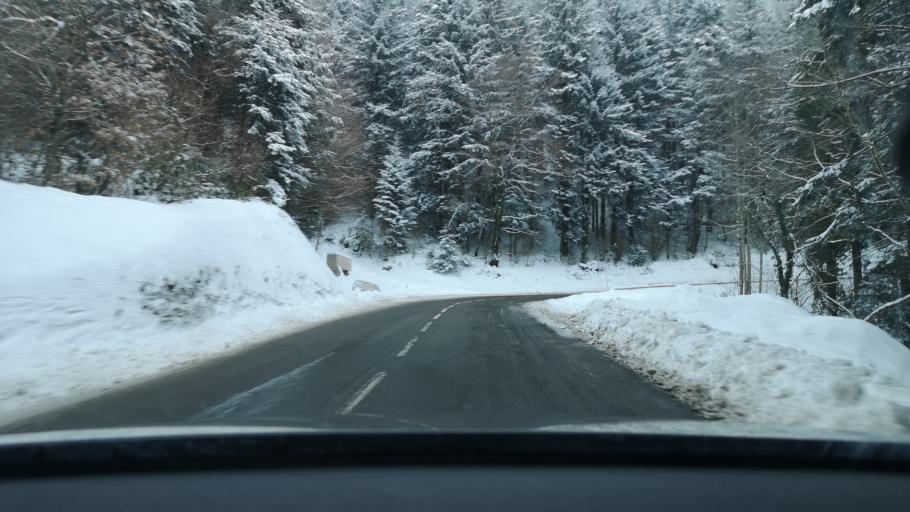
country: FR
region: Rhone-Alpes
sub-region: Departement de l'Ain
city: Arbent
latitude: 46.2540
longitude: 5.7055
